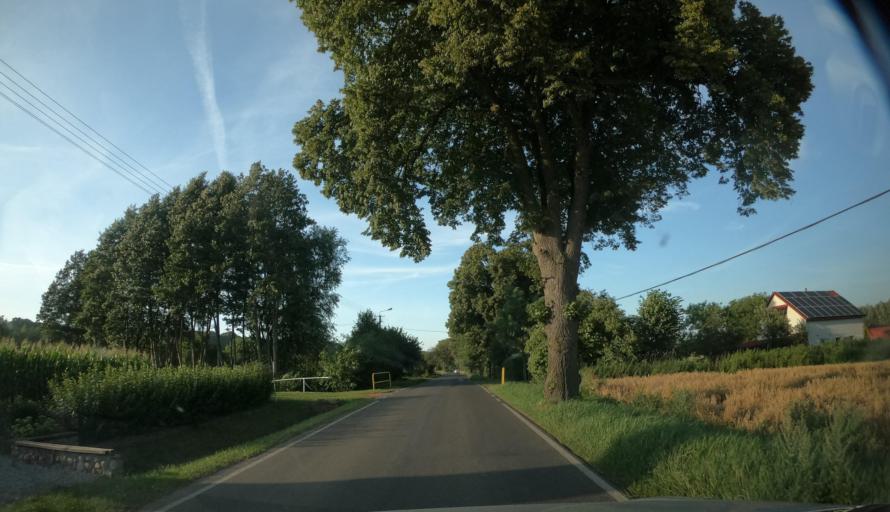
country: PL
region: Kujawsko-Pomorskie
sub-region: Bydgoszcz
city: Fordon
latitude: 53.2094
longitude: 18.1787
